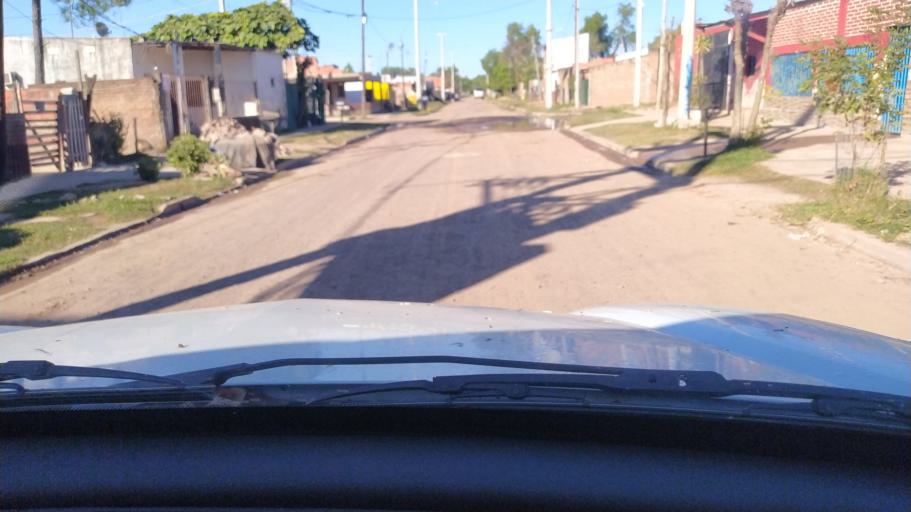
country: AR
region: Corrientes
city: Corrientes
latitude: -27.4942
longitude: -58.8090
